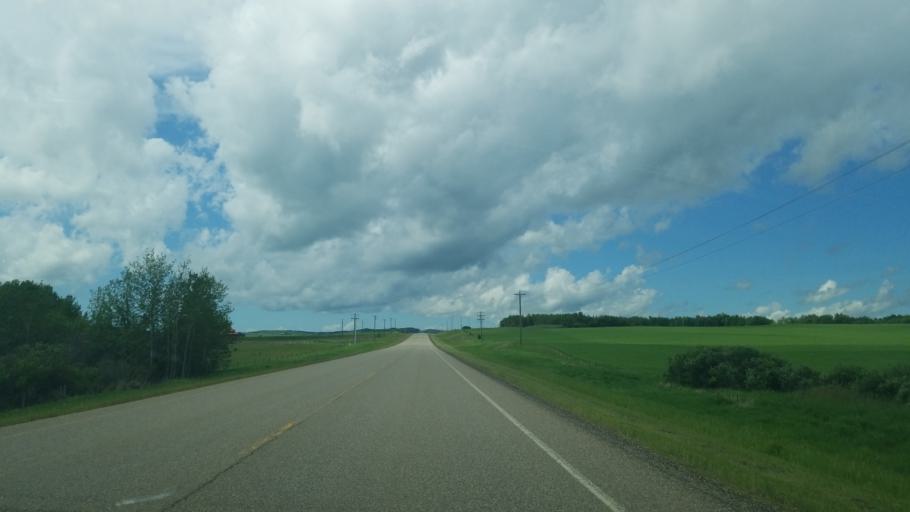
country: CA
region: Saskatchewan
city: Lloydminster
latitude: 53.1617
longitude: -110.1689
